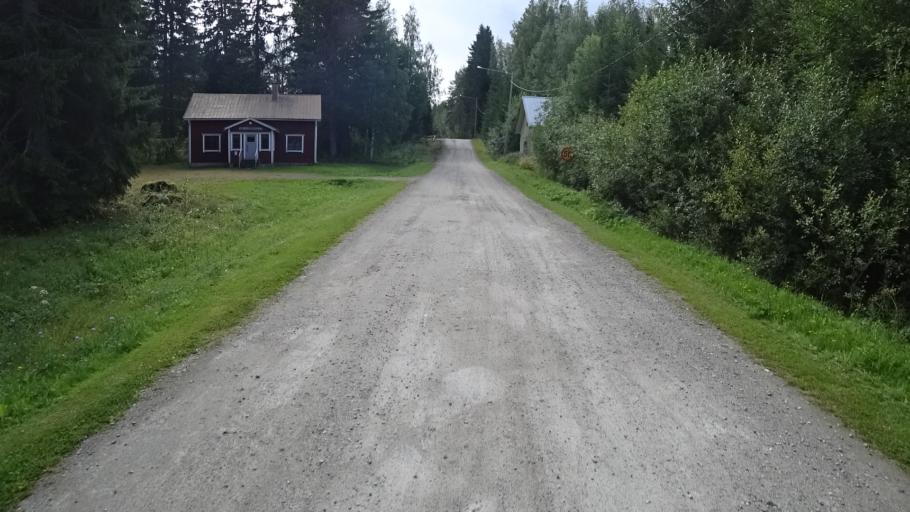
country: FI
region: North Karelia
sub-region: Joensuu
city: Ilomantsi
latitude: 62.6392
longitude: 31.2853
